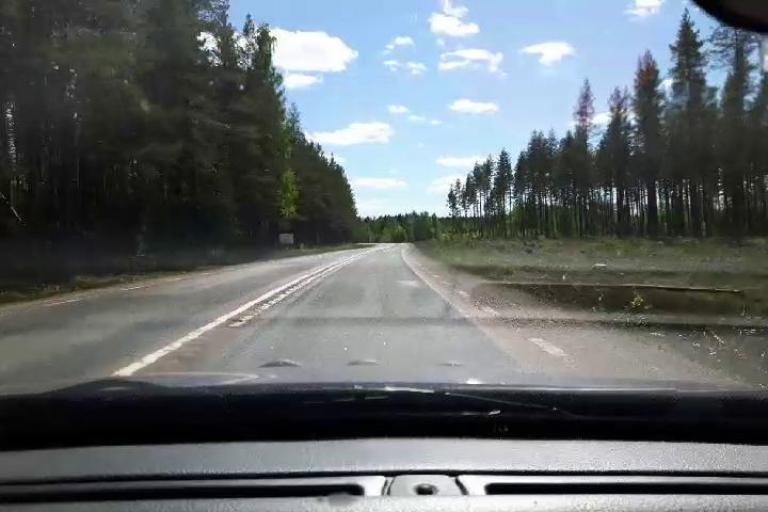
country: SE
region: Gaevleborg
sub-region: Ljusdals Kommun
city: Farila
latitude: 61.8363
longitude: 15.7514
